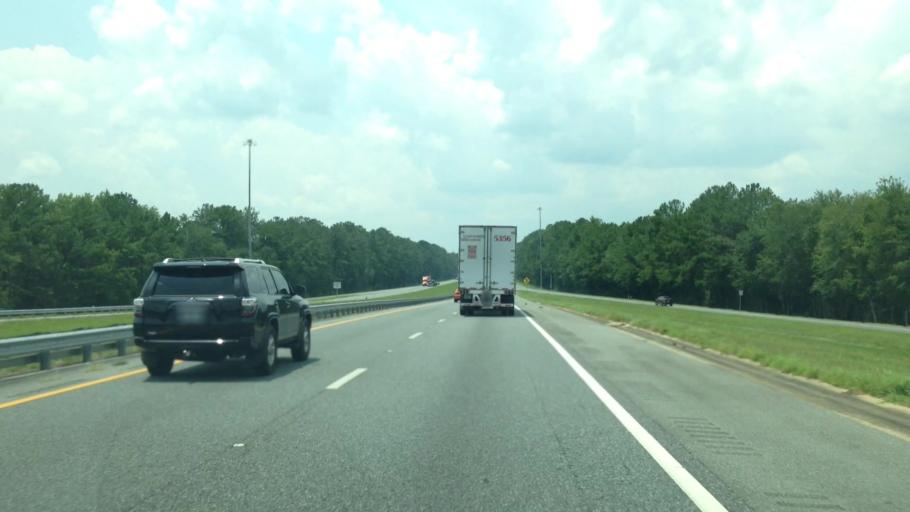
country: US
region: Florida
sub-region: Walton County
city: DeFuniak Springs
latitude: 30.7134
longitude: -85.9365
